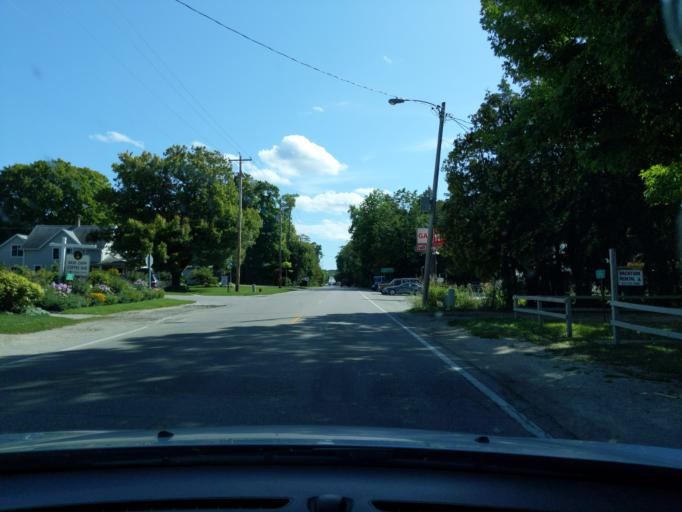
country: US
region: Wisconsin
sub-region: Door County
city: Sturgeon Bay
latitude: 45.2006
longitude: -87.1189
